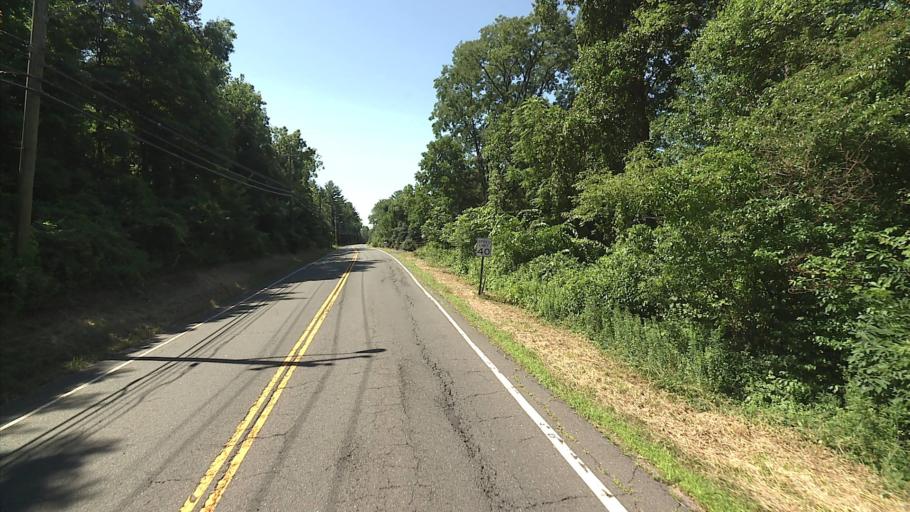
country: US
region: Connecticut
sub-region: Hartford County
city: Farmington
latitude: 41.7514
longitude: -72.8191
